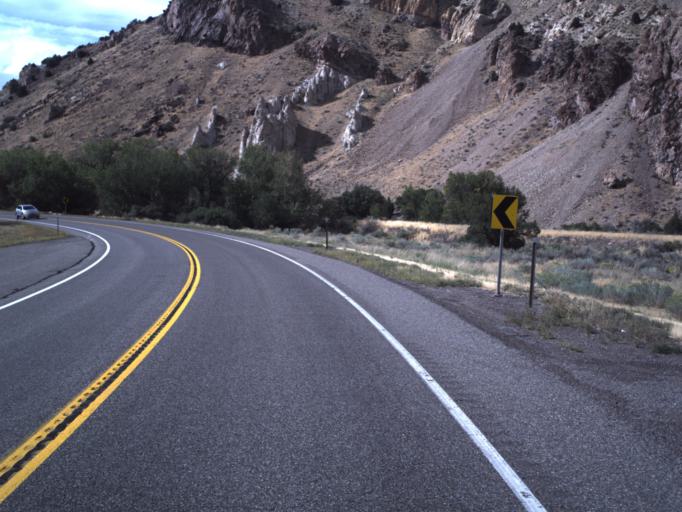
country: US
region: Utah
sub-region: Sevier County
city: Monroe
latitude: 38.5702
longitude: -112.2529
